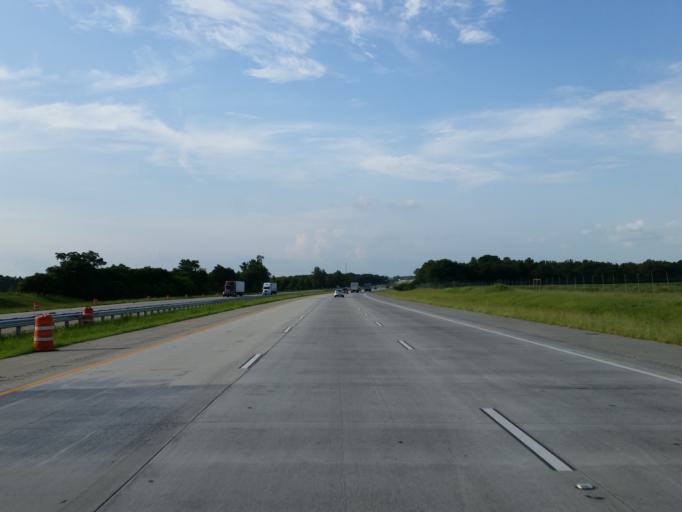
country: US
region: Georgia
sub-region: Dooly County
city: Unadilla
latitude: 32.2130
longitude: -83.7455
